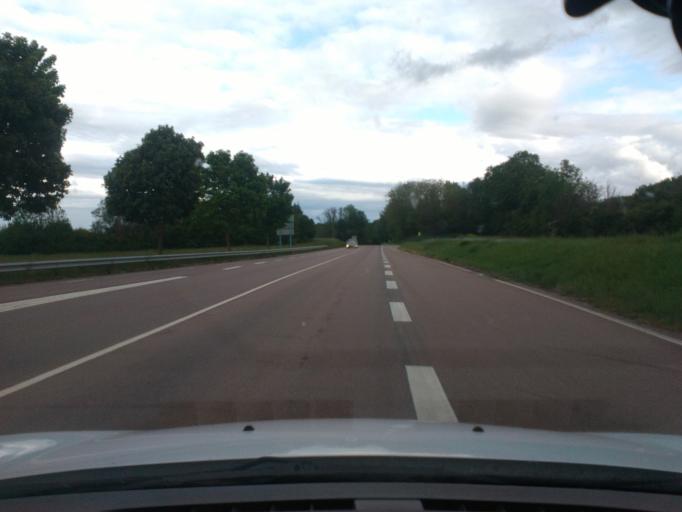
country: FR
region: Lorraine
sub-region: Departement des Vosges
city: Mirecourt
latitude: 48.3079
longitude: 6.0679
